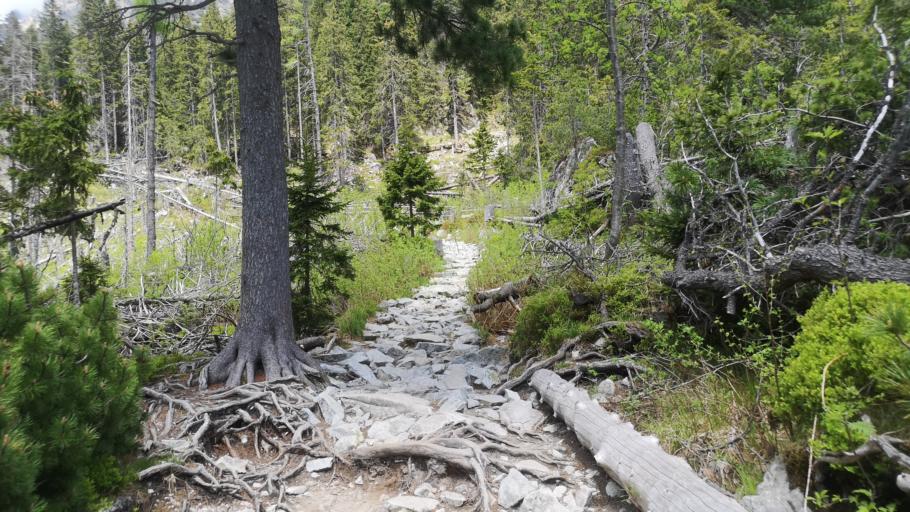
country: SK
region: Presovsky
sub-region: Okres Poprad
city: Vysoke Tatry
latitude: 49.1718
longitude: 20.2211
